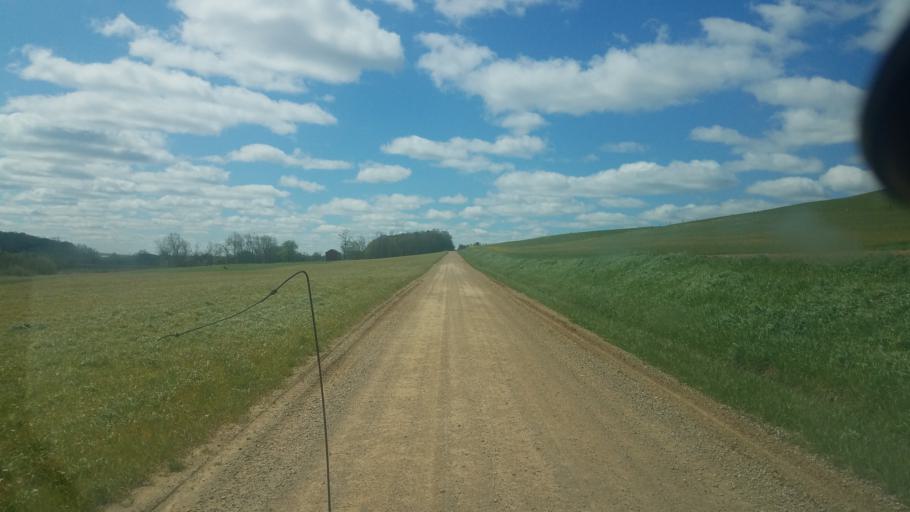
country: US
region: Ohio
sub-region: Knox County
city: Danville
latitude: 40.5261
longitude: -82.3051
